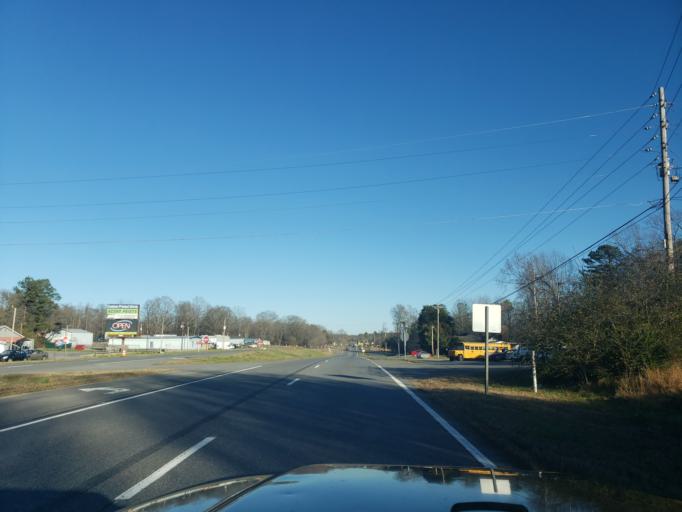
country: US
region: North Carolina
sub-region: Gaston County
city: Bessemer City
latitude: 35.2552
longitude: -81.2671
